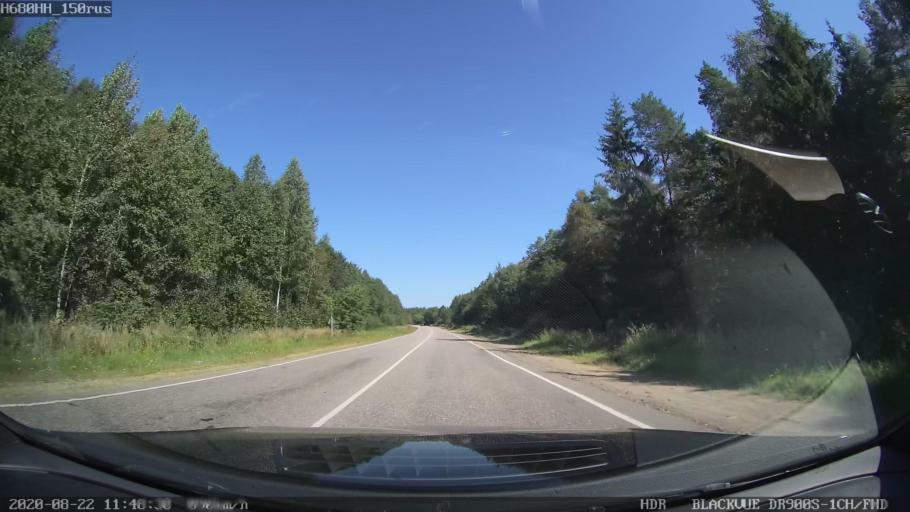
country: RU
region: Tverskaya
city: Sakharovo
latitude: 57.0635
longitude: 36.1041
